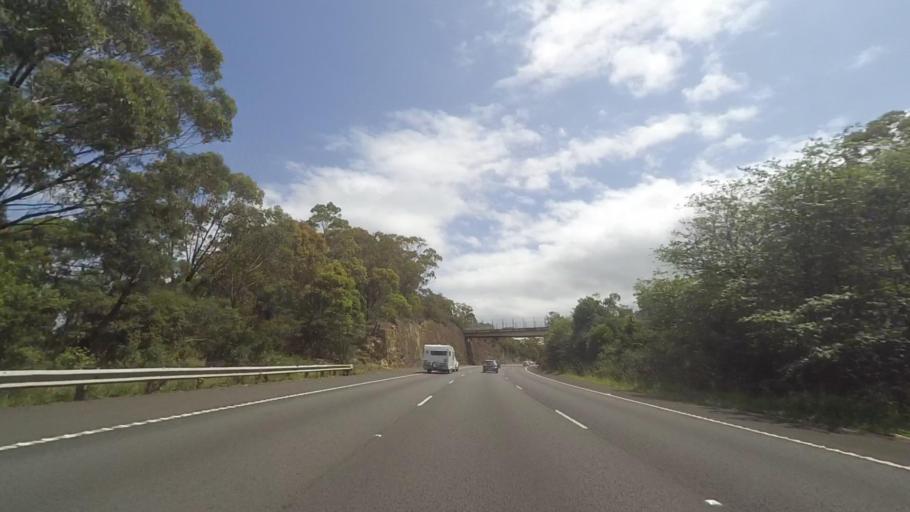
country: AU
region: New South Wales
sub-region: Gosford Shire
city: Lisarow
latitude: -33.3644
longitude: 151.3331
